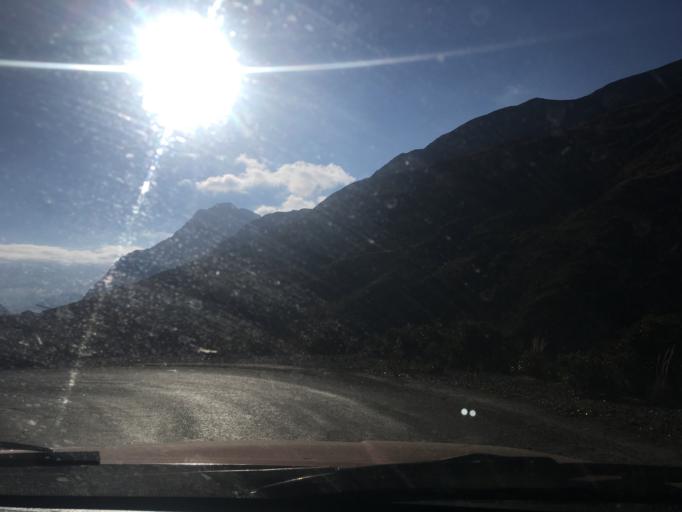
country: BO
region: La Paz
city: Quime
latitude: -17.0039
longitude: -67.2681
